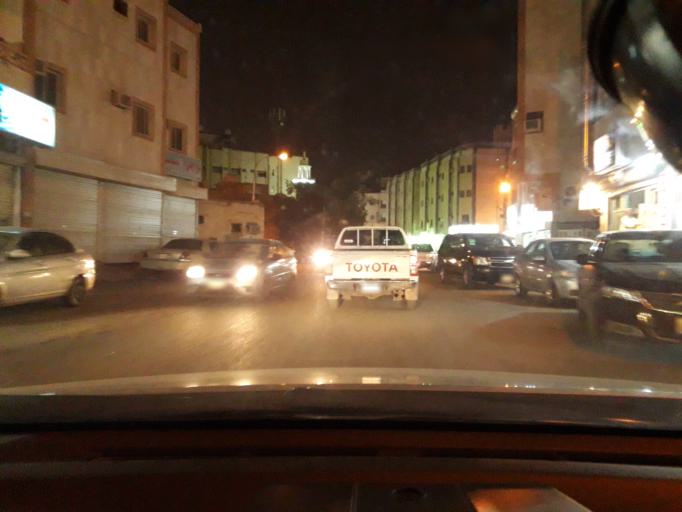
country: SA
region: Al Madinah al Munawwarah
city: Medina
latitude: 24.4665
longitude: 39.6280
